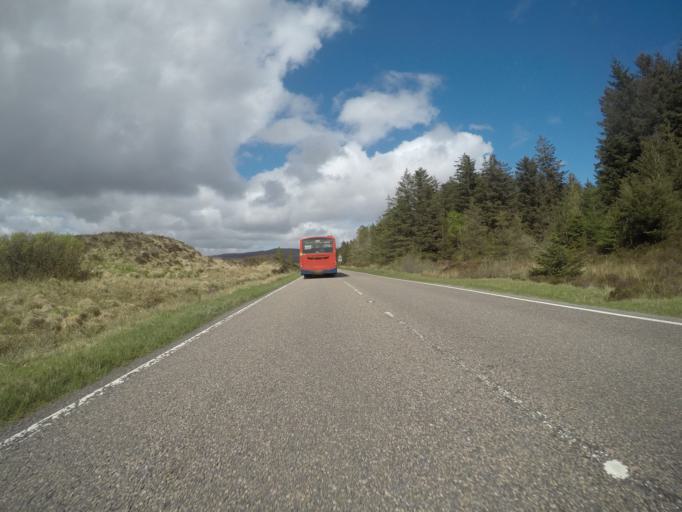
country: GB
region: Scotland
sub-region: Highland
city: Isle of Skye
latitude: 57.3101
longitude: -6.1934
